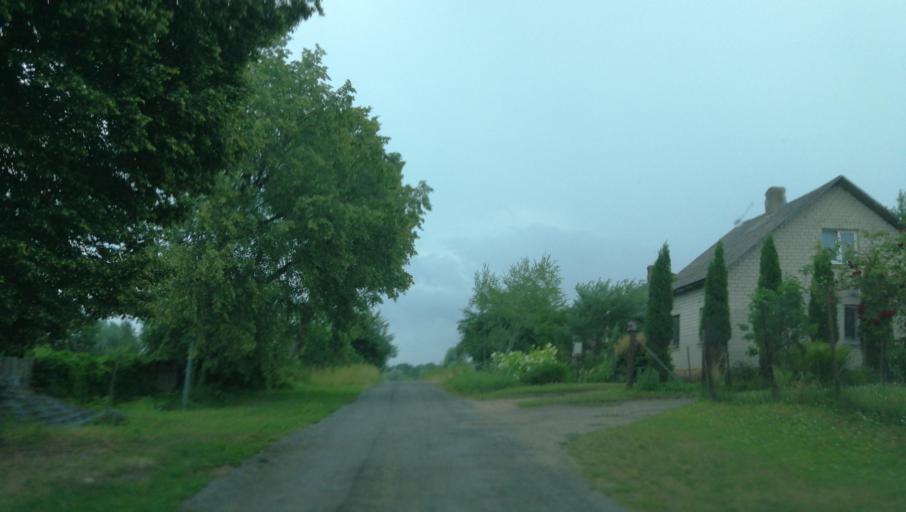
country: LV
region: Cesu Rajons
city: Cesis
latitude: 57.3206
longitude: 25.2698
